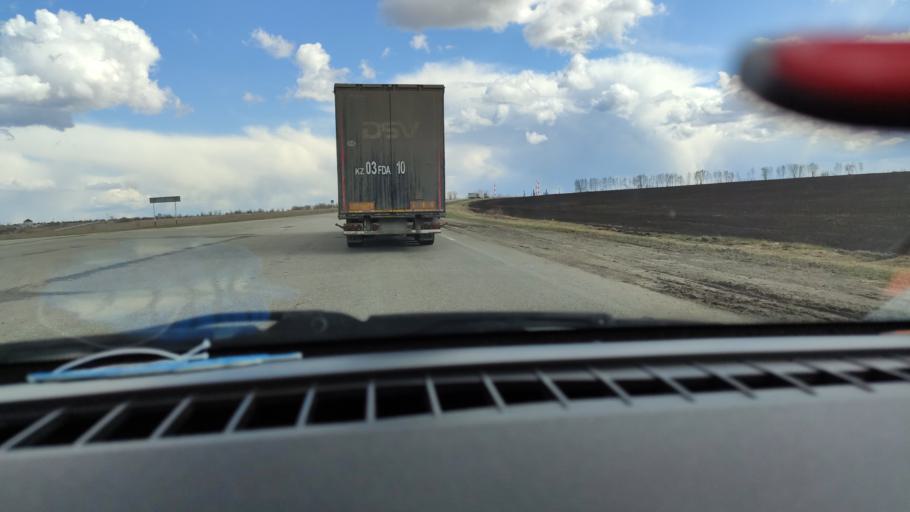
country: RU
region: Samara
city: Varlamovo
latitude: 53.1137
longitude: 48.3508
